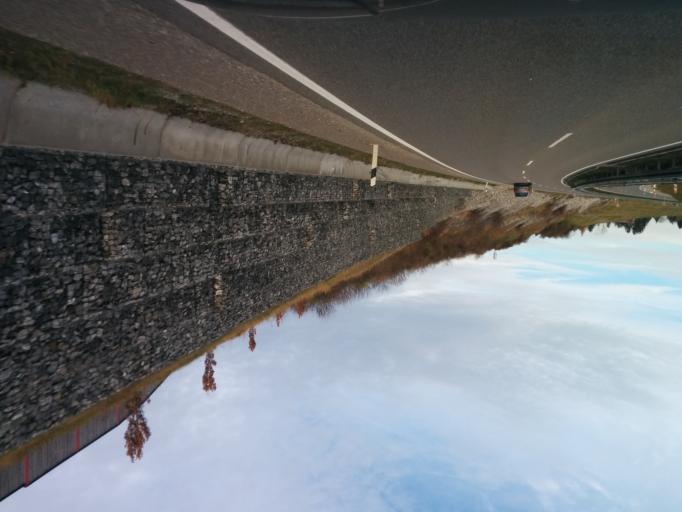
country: DE
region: Bavaria
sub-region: Swabia
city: Waltenhofen
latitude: 47.6722
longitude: 10.3004
